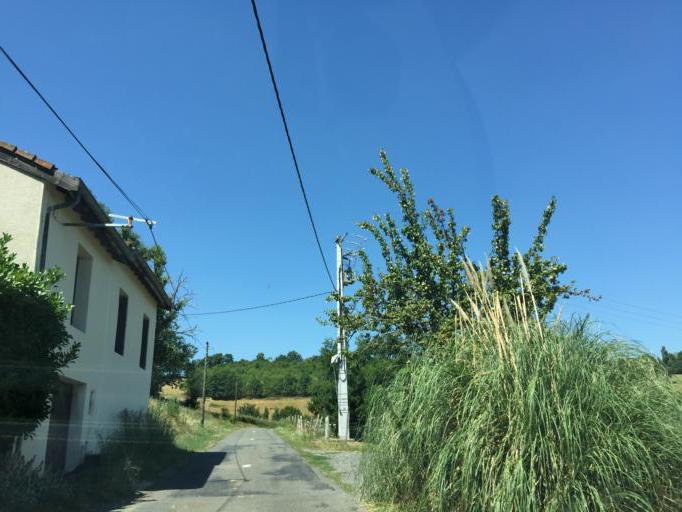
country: FR
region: Rhone-Alpes
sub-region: Departement de la Loire
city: Saint-Jean-Bonnefonds
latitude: 45.4635
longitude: 4.4580
